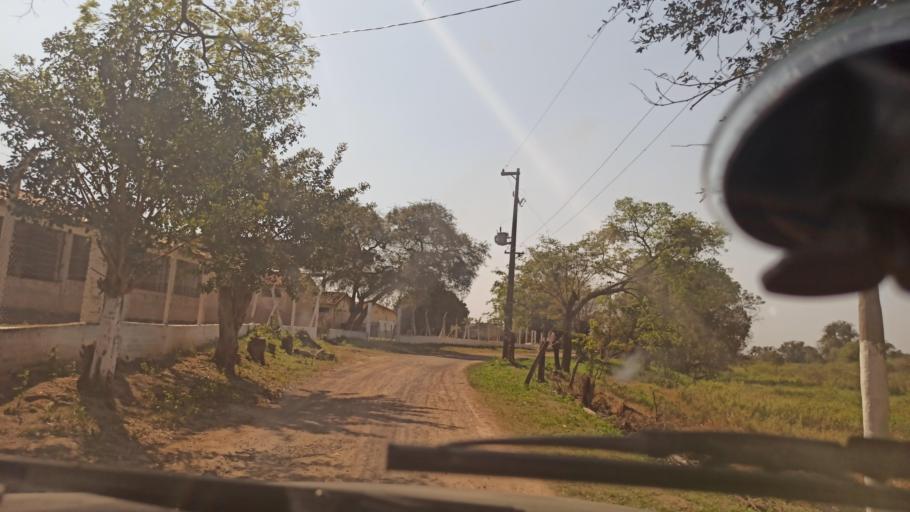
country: AR
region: Formosa
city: Clorinda
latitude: -25.3134
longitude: -57.6984
